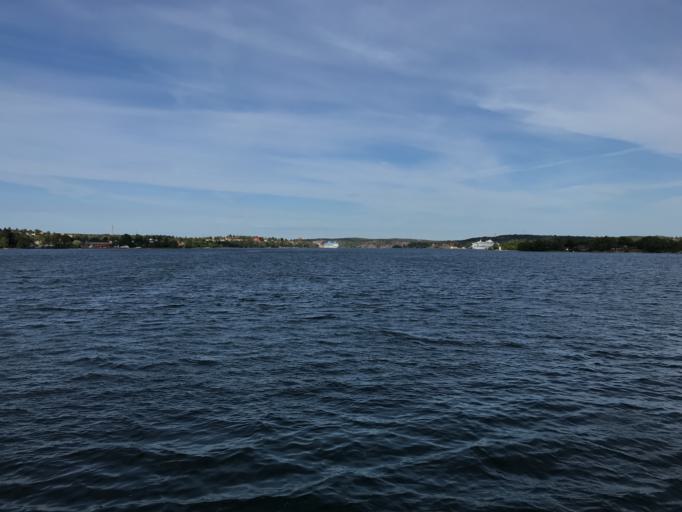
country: SE
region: Stockholm
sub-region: Nacka Kommun
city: Nacka
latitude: 59.3336
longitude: 18.1550
